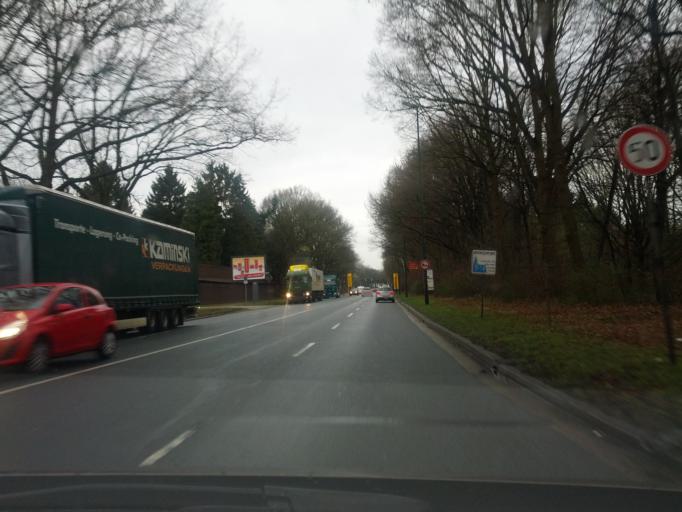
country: DE
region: Bremen
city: Bremen
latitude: 53.0505
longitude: 8.8119
